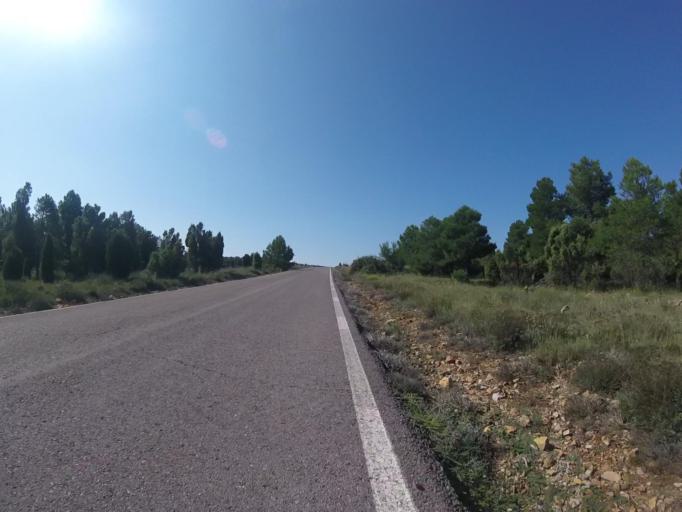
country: ES
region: Valencia
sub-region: Provincia de Castello
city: Benafigos
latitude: 40.2815
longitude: -0.2390
